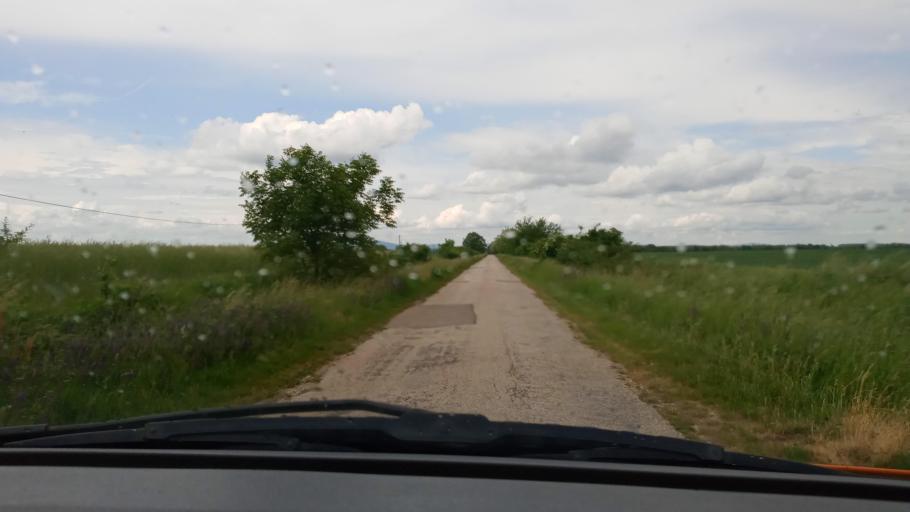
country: HU
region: Baranya
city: Harkany
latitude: 45.9060
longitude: 18.1385
